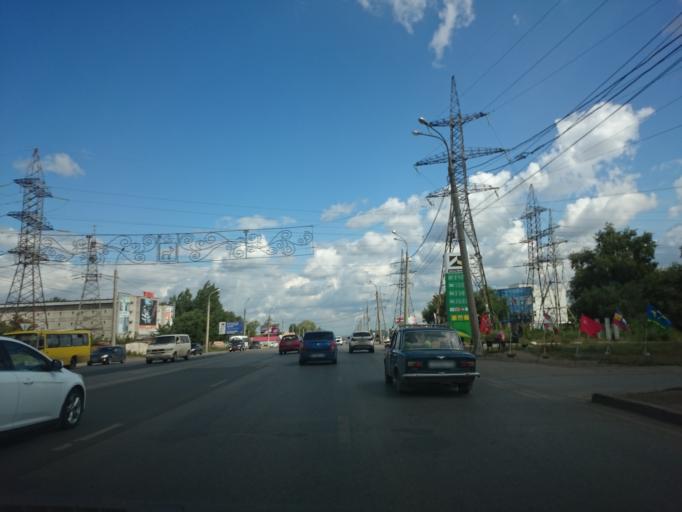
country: RU
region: Samara
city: Samara
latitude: 53.2612
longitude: 50.2395
